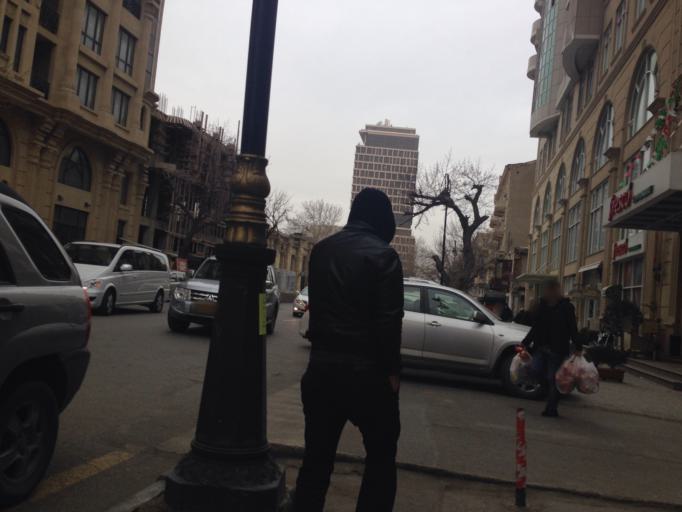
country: AZ
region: Baki
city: Baku
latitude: 40.3772
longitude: 49.8546
